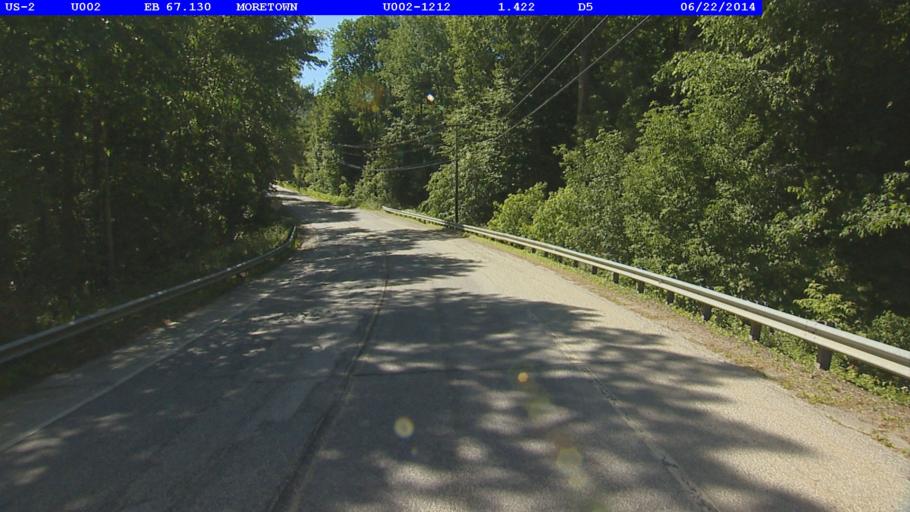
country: US
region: Vermont
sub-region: Washington County
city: Waterbury
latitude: 44.3142
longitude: -72.7251
